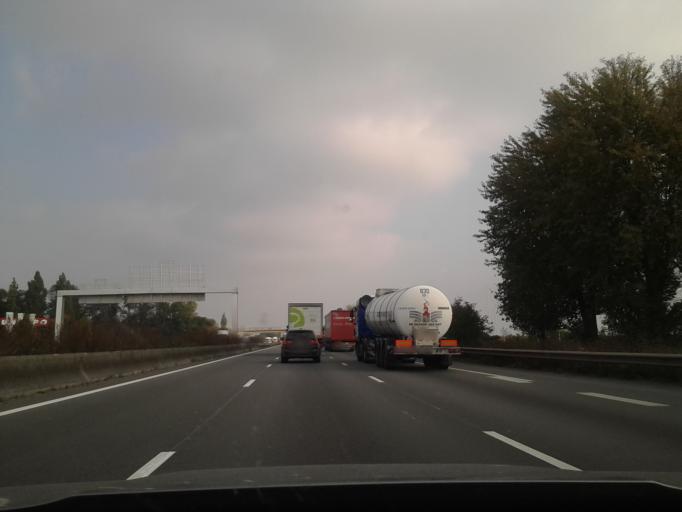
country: FR
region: Nord-Pas-de-Calais
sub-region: Departement du Nord
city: Avelin
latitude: 50.5488
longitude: 3.0588
